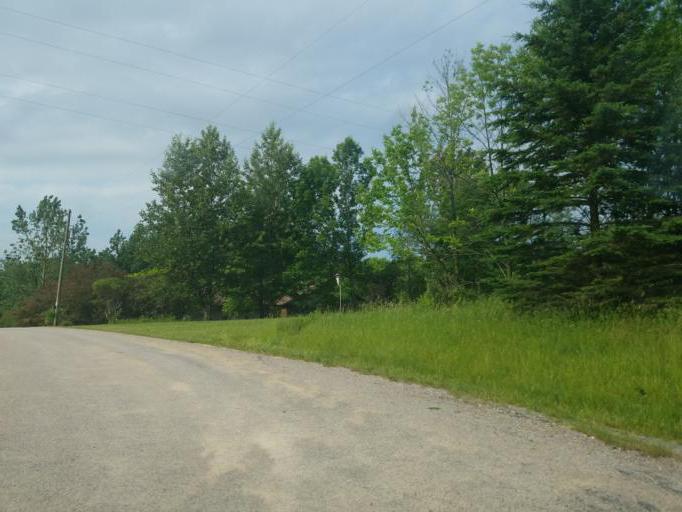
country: US
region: Wisconsin
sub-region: Vernon County
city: Hillsboro
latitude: 43.5969
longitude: -90.4167
